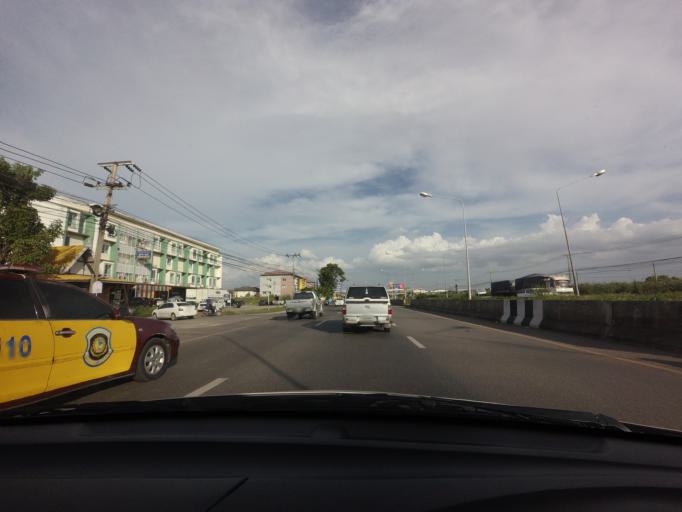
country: TH
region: Nonthaburi
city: Bang Bua Thong
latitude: 13.9668
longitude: 100.3986
